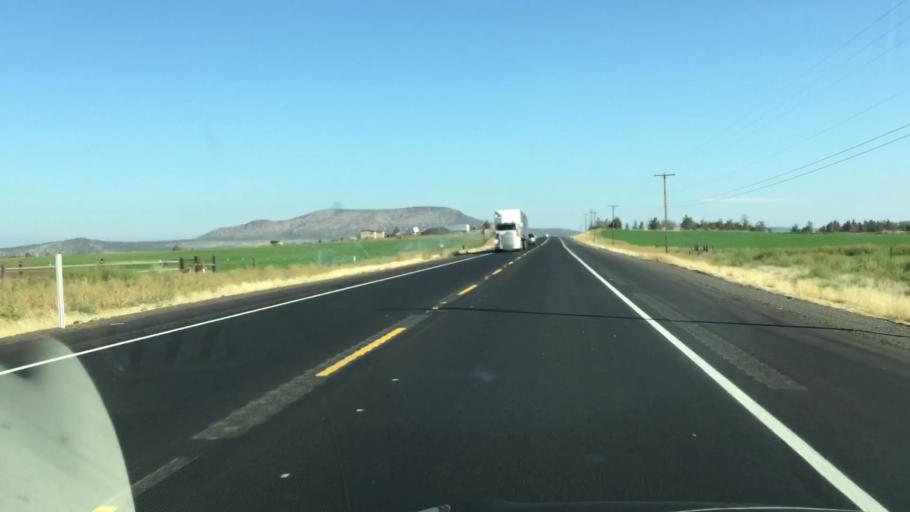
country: US
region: Oregon
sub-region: Deschutes County
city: Terrebonne
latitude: 44.4221
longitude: -121.1992
